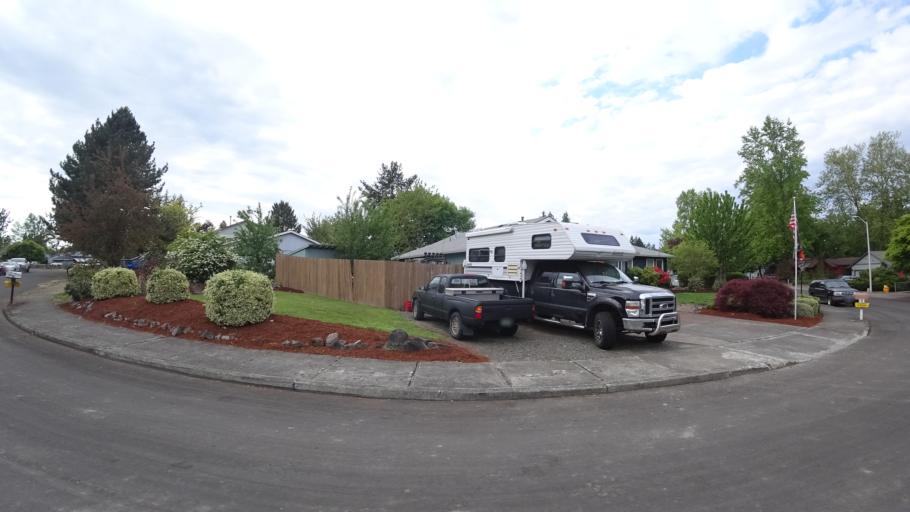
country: US
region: Oregon
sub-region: Washington County
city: Hillsboro
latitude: 45.4963
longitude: -122.9501
